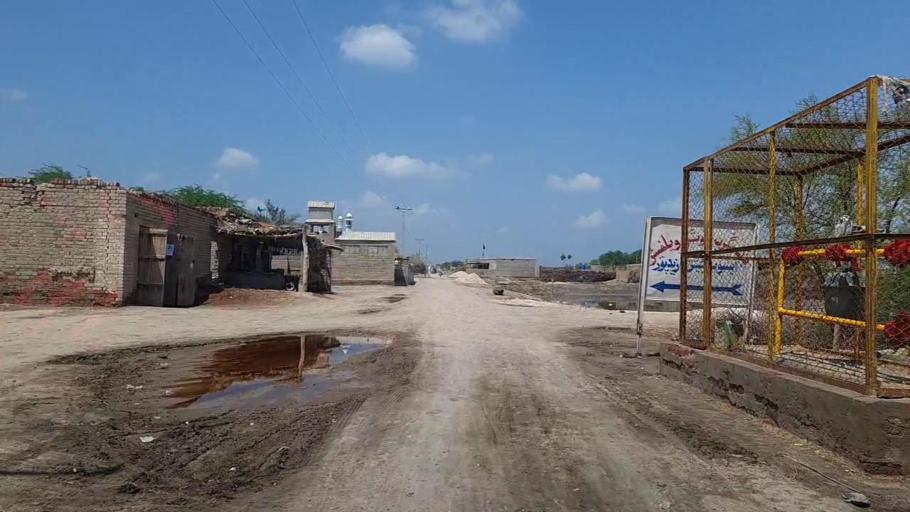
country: PK
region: Sindh
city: Kandiaro
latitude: 26.9999
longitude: 68.2553
